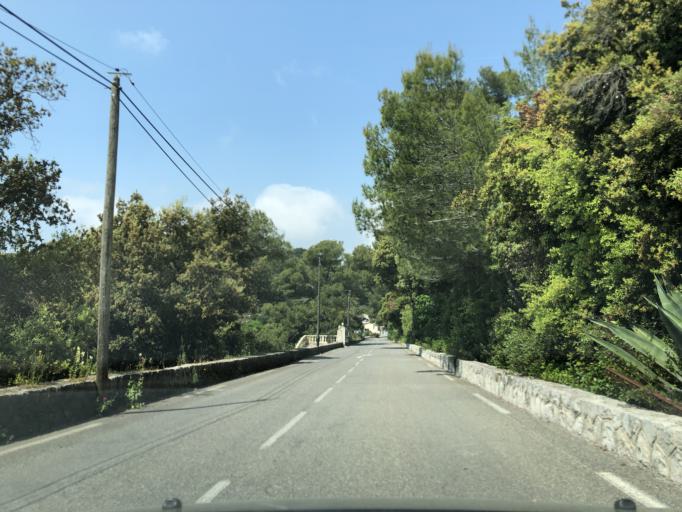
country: FR
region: Provence-Alpes-Cote d'Azur
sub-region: Departement des Alpes-Maritimes
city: Villefranche-sur-Mer
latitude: 43.7169
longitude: 7.3161
